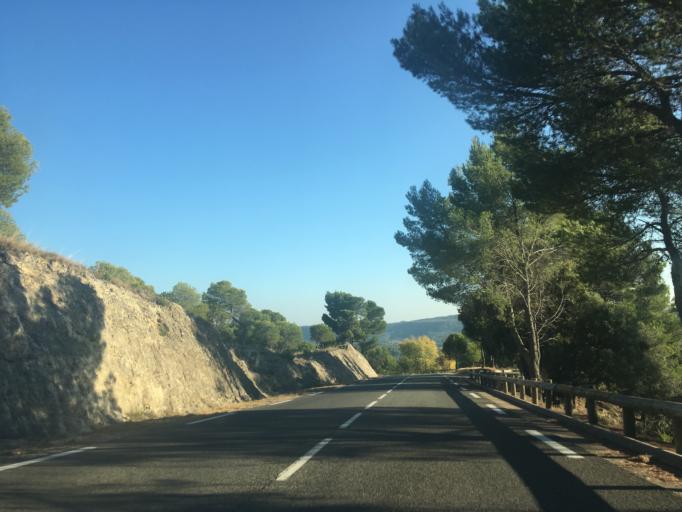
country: FR
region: Provence-Alpes-Cote d'Azur
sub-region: Departement du Var
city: Villecroze
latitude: 43.5862
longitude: 6.2659
